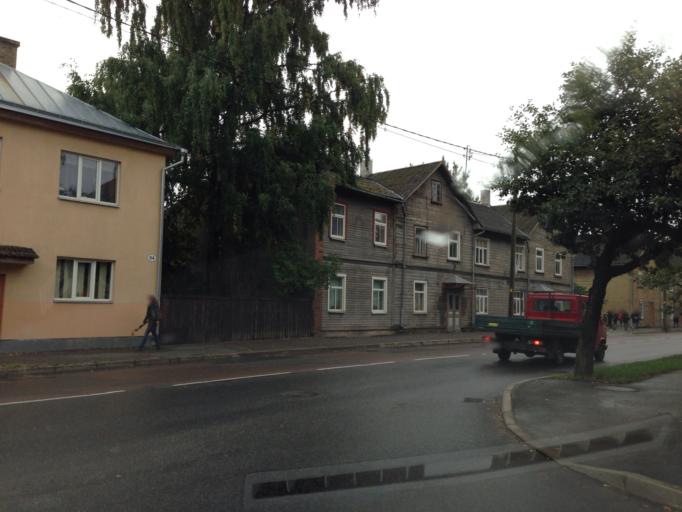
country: EE
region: Tartu
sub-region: Tartu linn
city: Tartu
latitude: 58.3692
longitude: 26.7212
